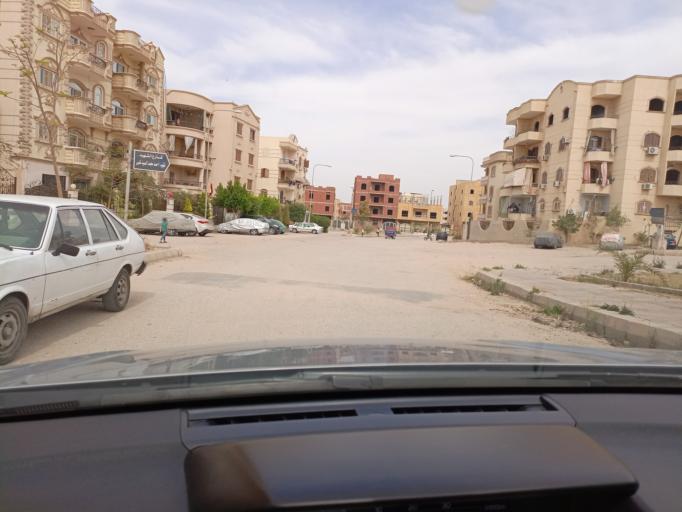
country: EG
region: Muhafazat al Qalyubiyah
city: Al Khankah
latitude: 30.2443
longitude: 31.4881
